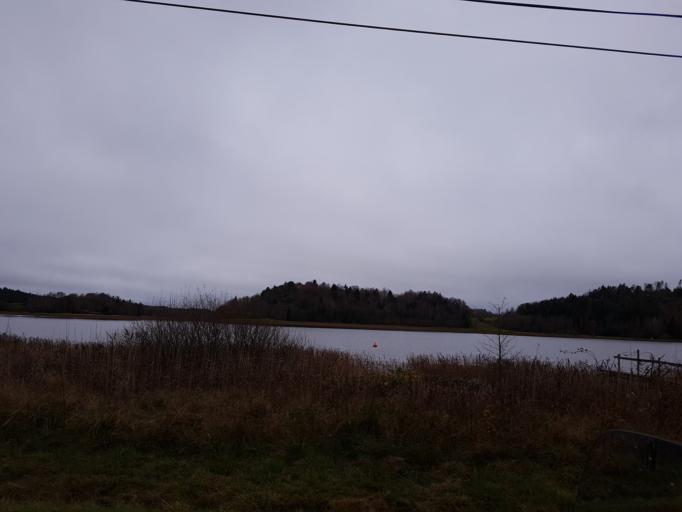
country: SE
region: Vaestra Goetaland
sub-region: Orust
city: Henan
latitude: 58.2341
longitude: 11.7616
